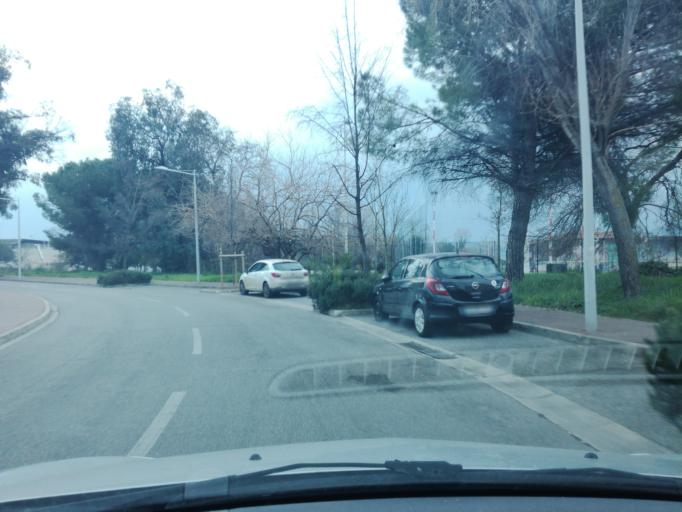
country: FR
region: Provence-Alpes-Cote d'Azur
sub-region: Departement des Alpes-Maritimes
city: Mandelieu-la-Napoule
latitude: 43.5549
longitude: 6.9631
